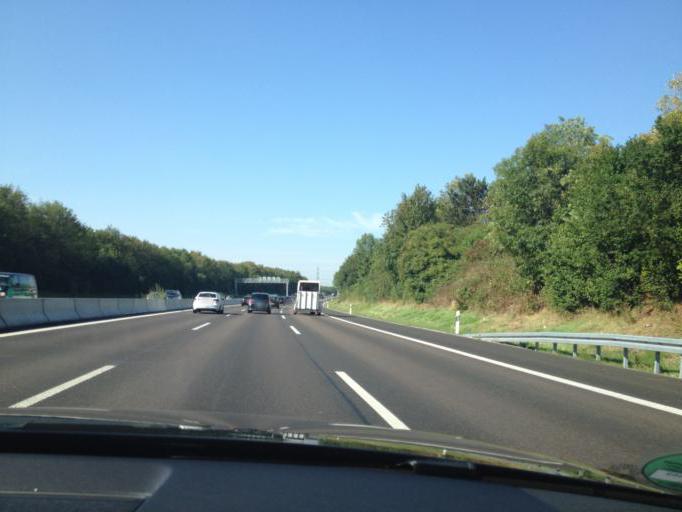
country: DE
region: Baden-Wuerttemberg
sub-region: Regierungsbezirk Stuttgart
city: Freiberg am Neckar
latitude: 48.9330
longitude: 9.1852
